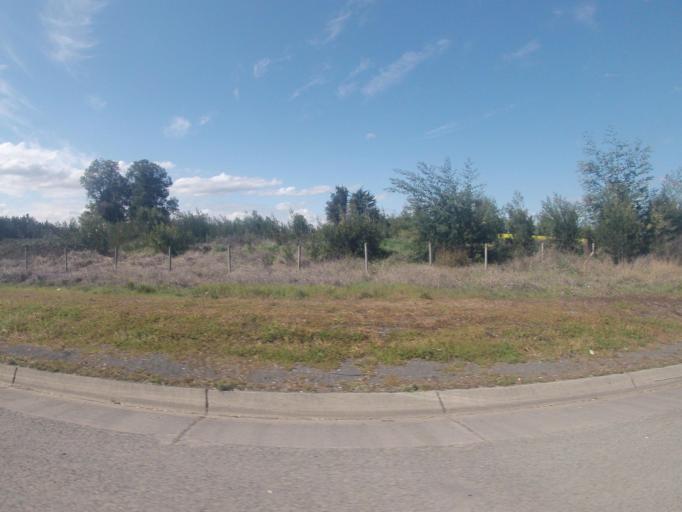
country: CL
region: Biobio
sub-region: Provincia de Biobio
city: Los Angeles
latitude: -37.4464
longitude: -72.4041
